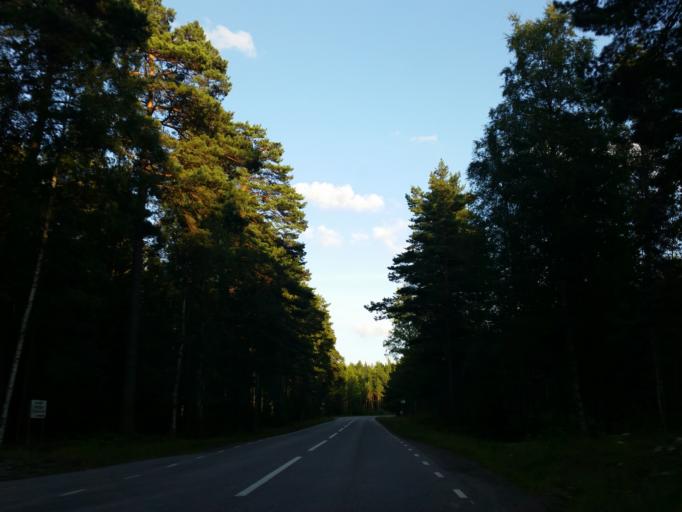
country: SE
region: Stockholm
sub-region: Sodertalje Kommun
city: Soedertaelje
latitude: 59.2466
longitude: 17.5377
